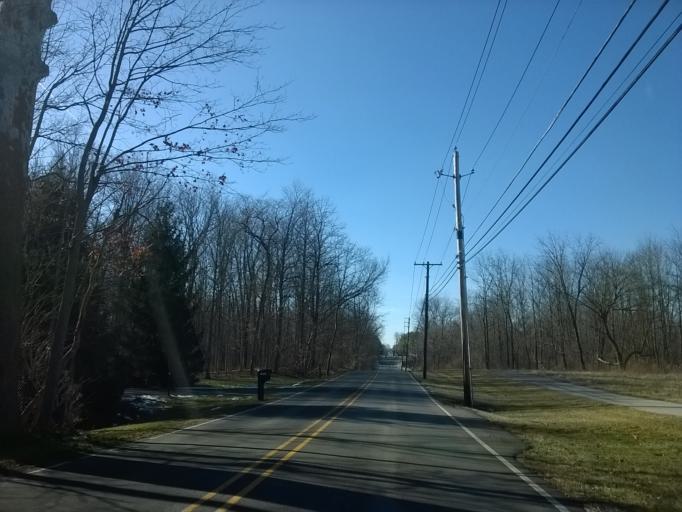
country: US
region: Indiana
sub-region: Marion County
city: Meridian Hills
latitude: 39.9415
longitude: -86.1861
